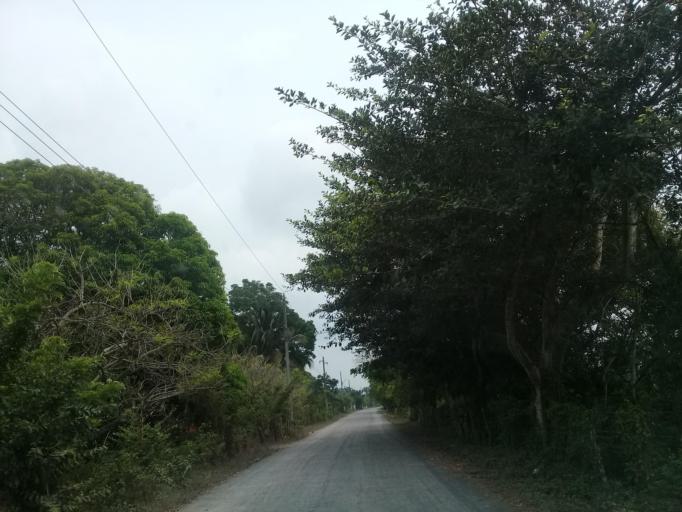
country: MX
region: Veracruz
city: El Tejar
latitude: 19.0548
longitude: -96.1982
